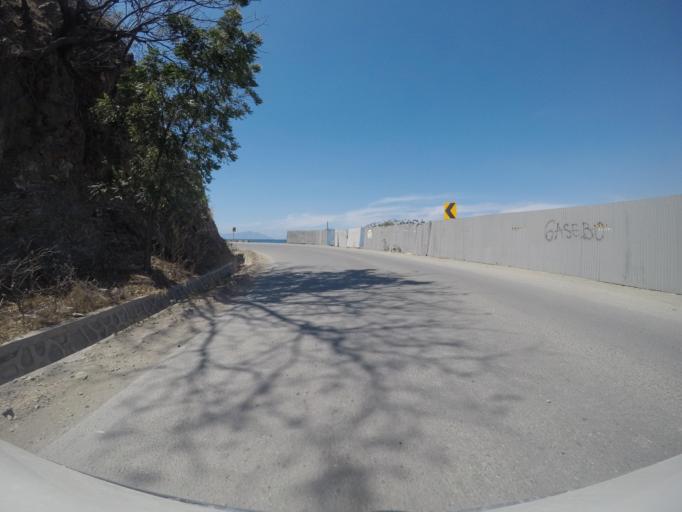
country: TL
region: Dili
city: Dili
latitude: -8.5689
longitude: 125.4721
